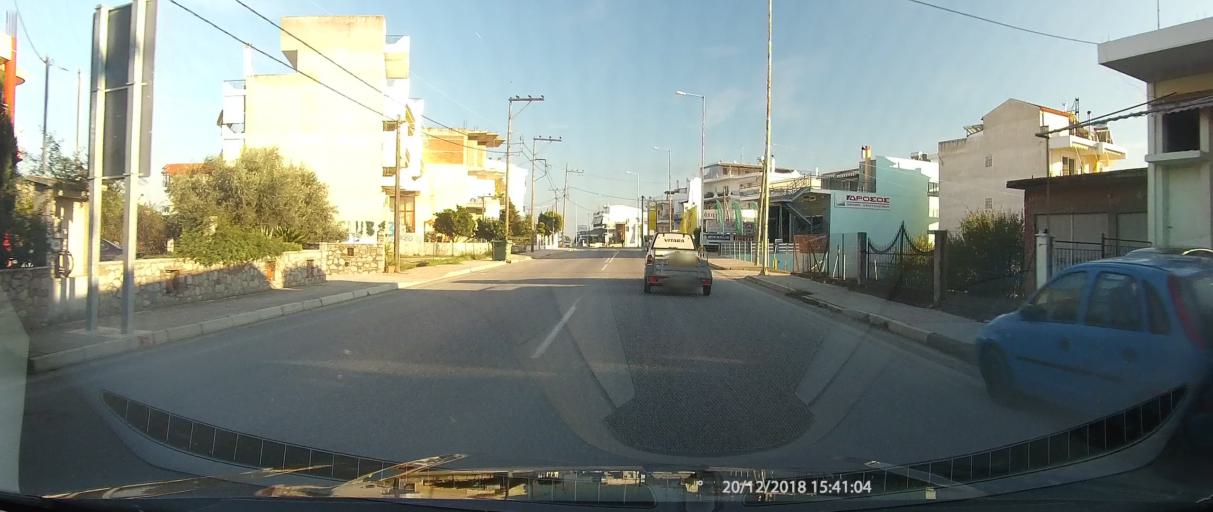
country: GR
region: Central Greece
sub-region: Nomos Fthiotidos
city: Stavros
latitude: 38.8911
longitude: 22.3805
